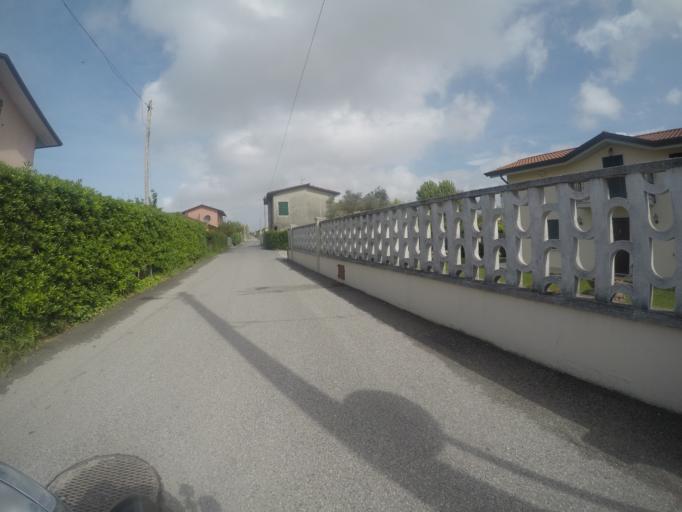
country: IT
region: Tuscany
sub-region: Provincia di Massa-Carrara
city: Massa
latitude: 44.0217
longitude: 10.0886
